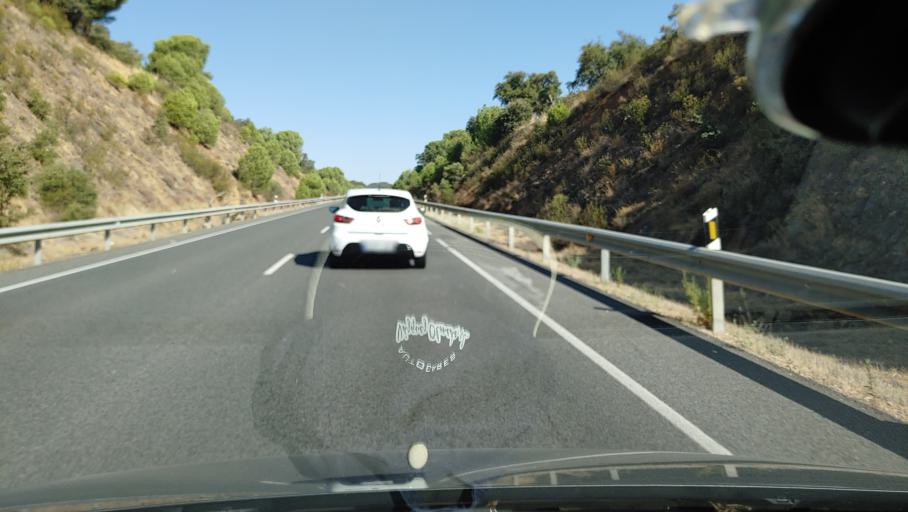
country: ES
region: Andalusia
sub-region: Province of Cordoba
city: Cordoba
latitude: 38.0058
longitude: -4.8013
